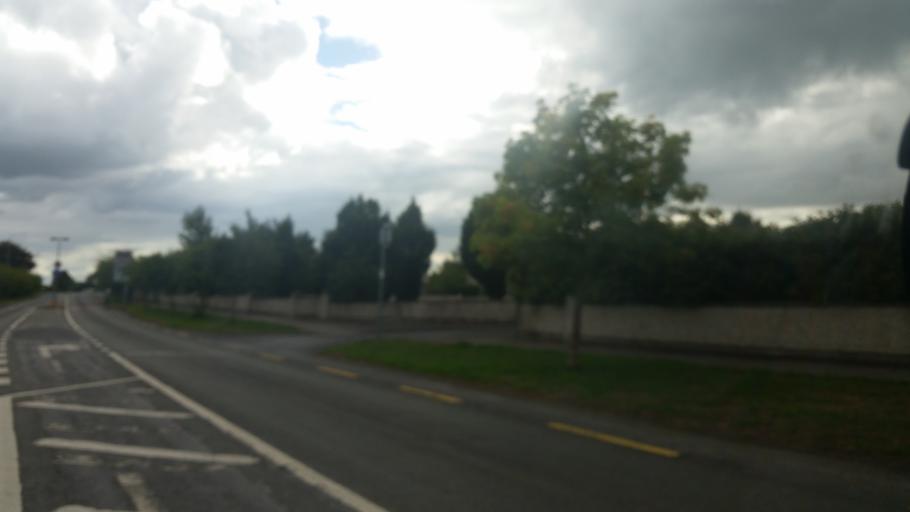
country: IE
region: Leinster
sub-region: County Carlow
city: Bagenalstown
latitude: 52.6779
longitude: -7.0220
